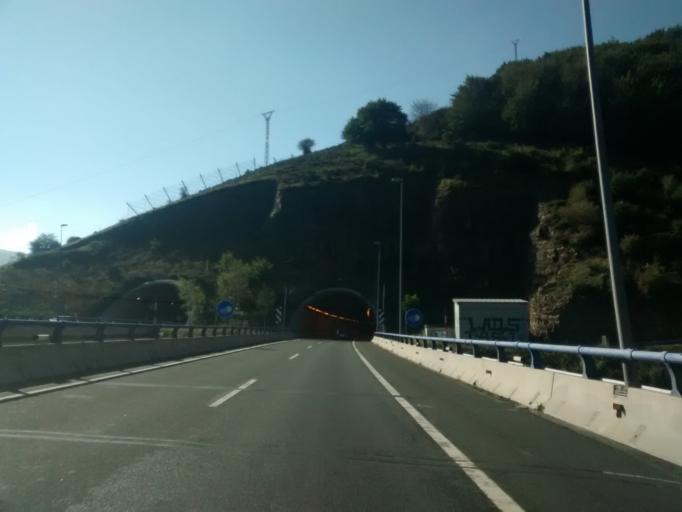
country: ES
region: Cantabria
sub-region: Provincia de Cantabria
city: Santiurde de Reinosa
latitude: 43.0533
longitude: -4.0868
